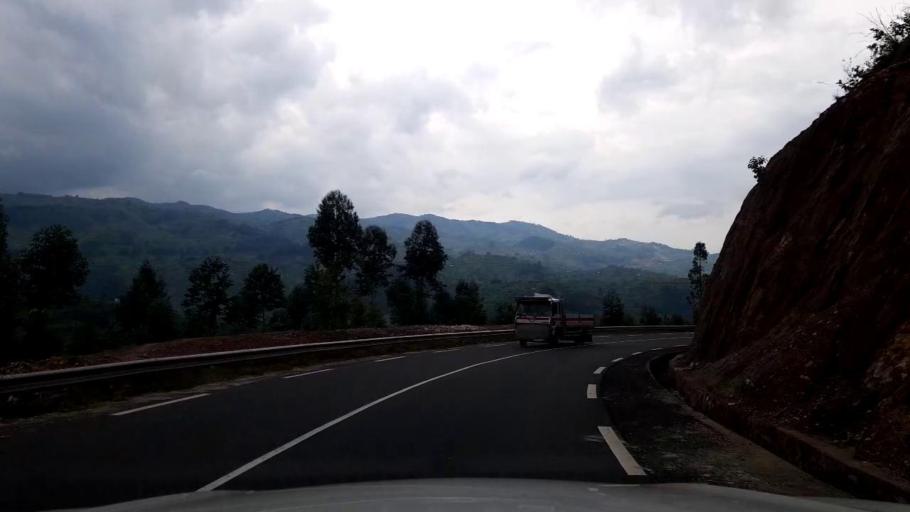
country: RW
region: Western Province
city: Kibuye
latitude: -1.9060
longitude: 29.3660
